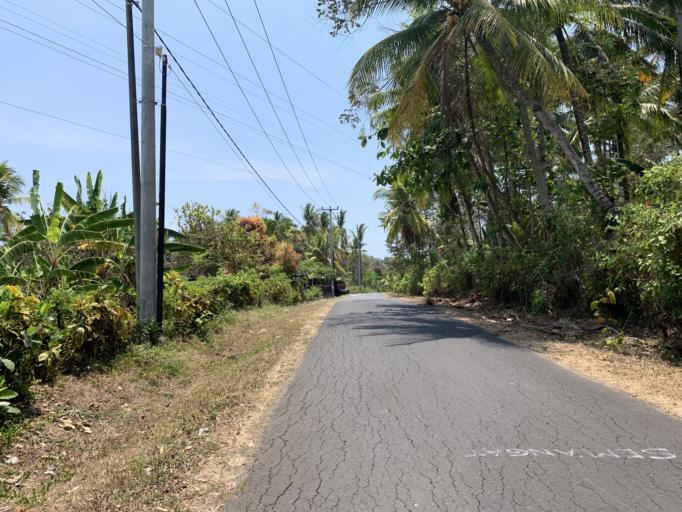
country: ID
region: Bali
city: Banjar Dangin Pangkung
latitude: -8.4315
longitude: 114.8335
